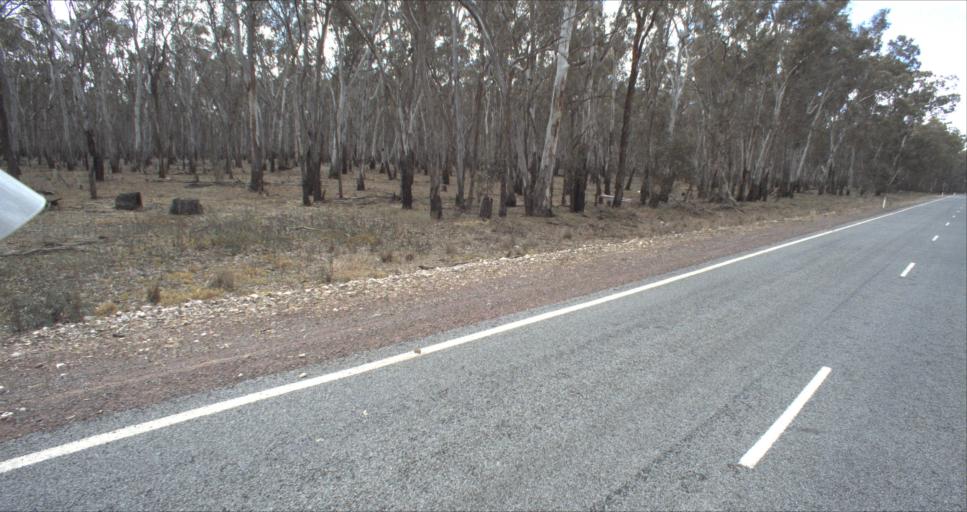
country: AU
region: New South Wales
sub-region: Leeton
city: Leeton
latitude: -34.6276
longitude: 146.3781
